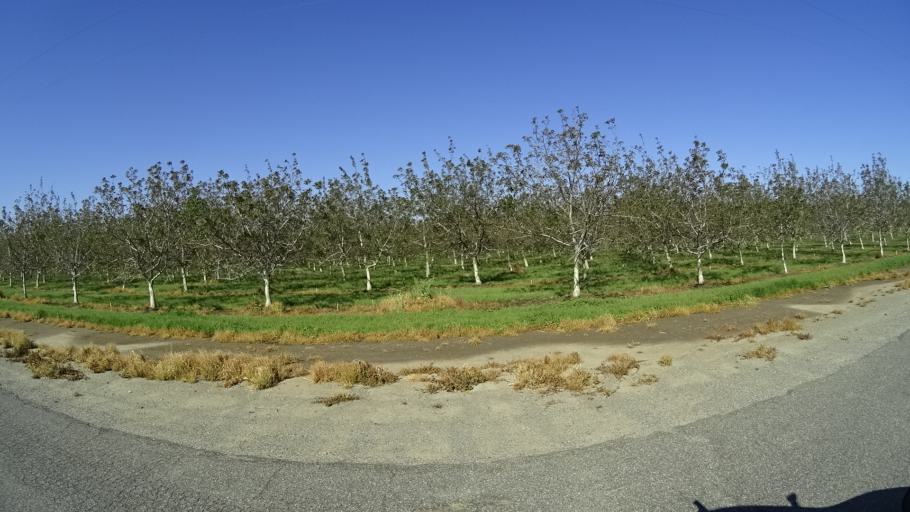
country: US
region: California
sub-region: Glenn County
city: Hamilton City
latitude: 39.6862
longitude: -122.0743
